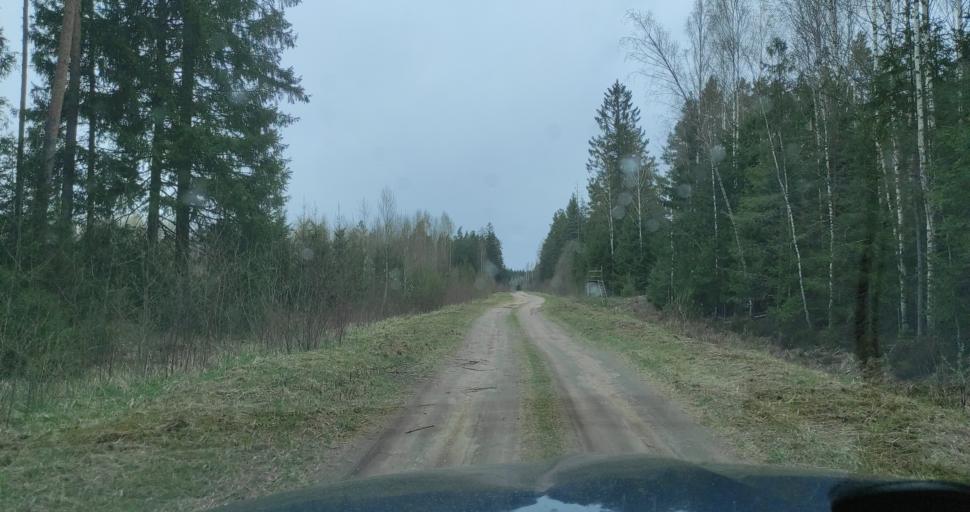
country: LV
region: Dundaga
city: Dundaga
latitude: 57.3573
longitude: 22.1533
